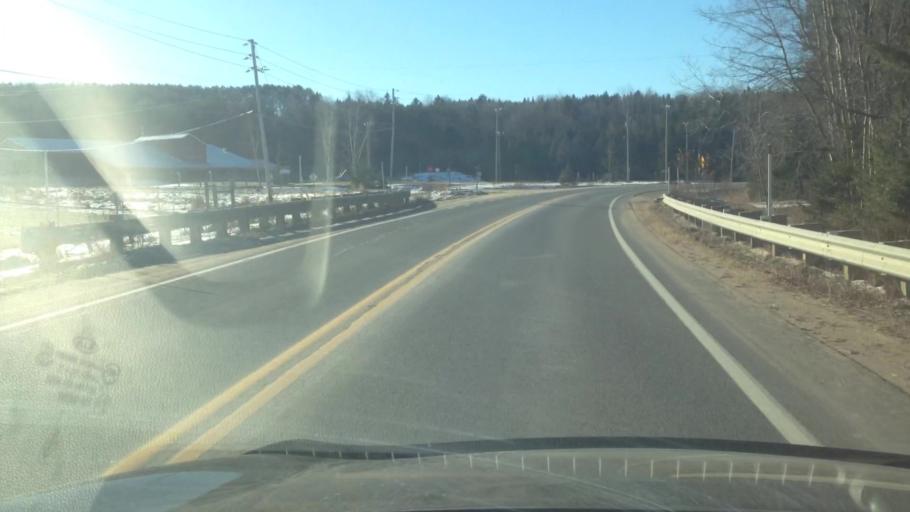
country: CA
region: Quebec
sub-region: Laurentides
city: Mont-Tremblant
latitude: 45.9612
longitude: -74.6008
